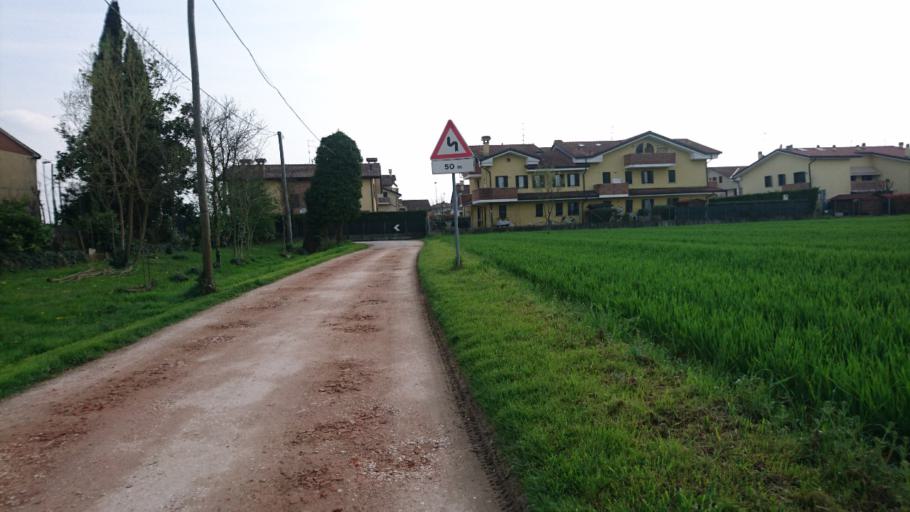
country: IT
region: Veneto
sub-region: Provincia di Padova
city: San Vito
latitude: 45.4163
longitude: 11.9777
